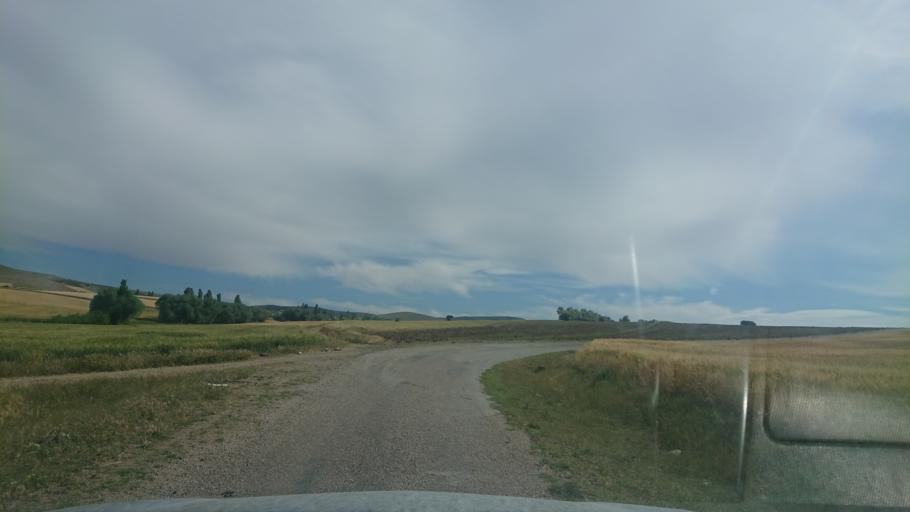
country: TR
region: Aksaray
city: Ortakoy
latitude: 38.8172
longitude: 34.0027
